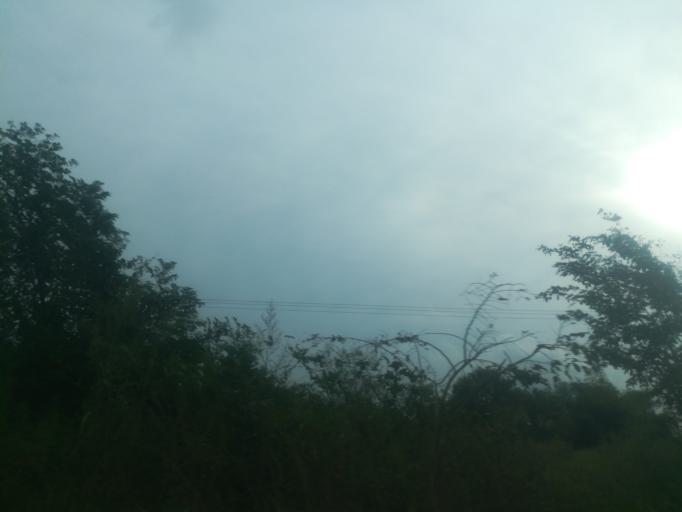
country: NG
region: Ogun
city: Ayetoro
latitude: 7.2372
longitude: 3.1303
